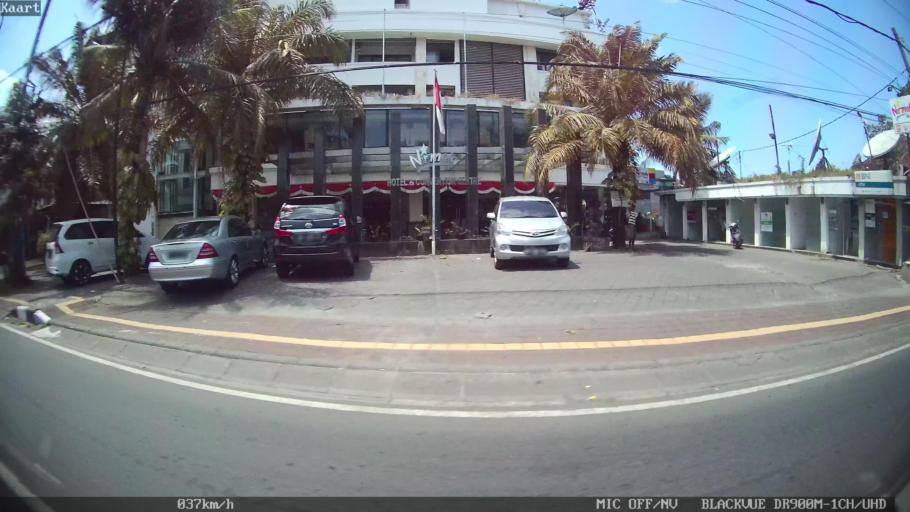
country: ID
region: Bali
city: Denpasar
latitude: -8.6593
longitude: 115.1911
